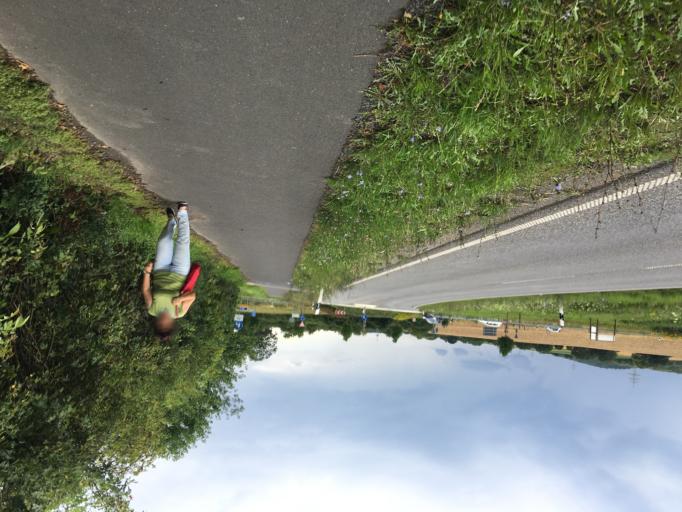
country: DE
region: Hesse
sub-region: Regierungsbezirk Darmstadt
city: Gelnhausen
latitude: 50.1869
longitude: 9.1904
